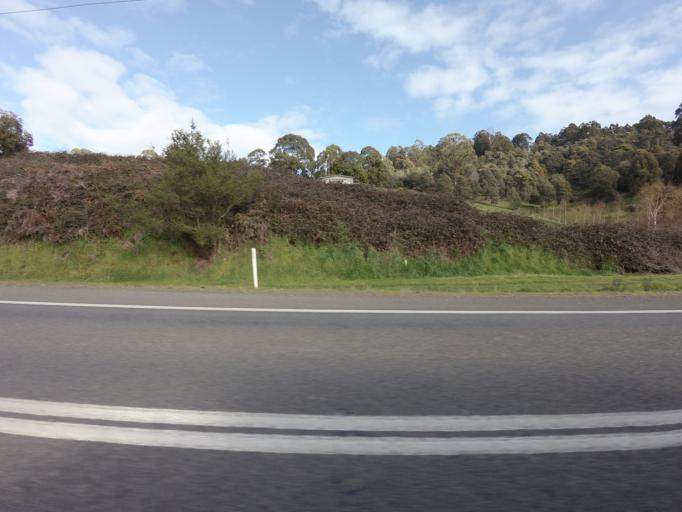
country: AU
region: Tasmania
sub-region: Huon Valley
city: Franklin
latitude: -43.1054
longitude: 147.0003
